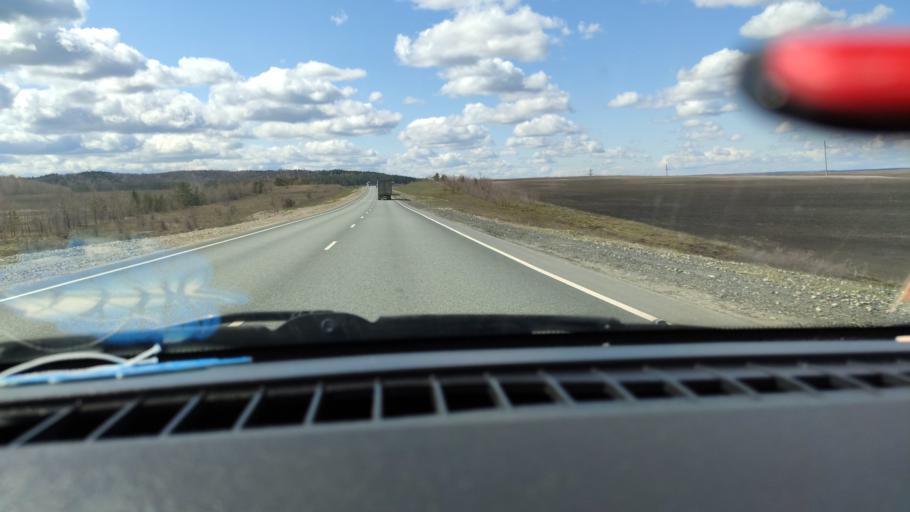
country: RU
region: Saratov
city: Khvalynsk
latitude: 52.5499
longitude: 48.0733
